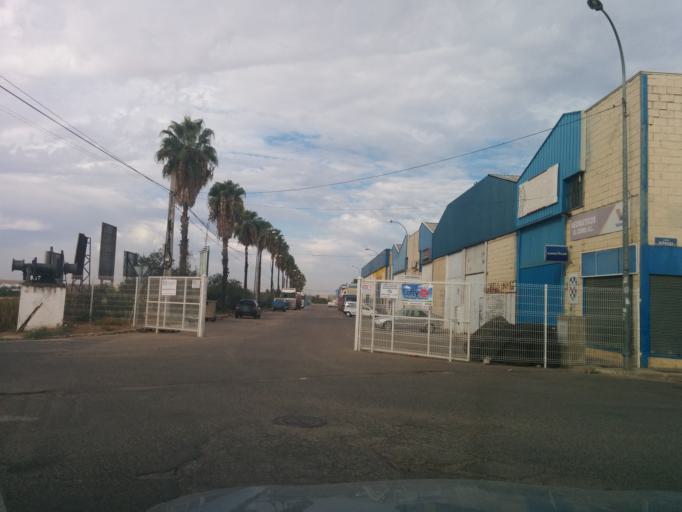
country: ES
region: Andalusia
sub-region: Provincia de Sevilla
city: Guillena
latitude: 37.5545
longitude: -6.0362
